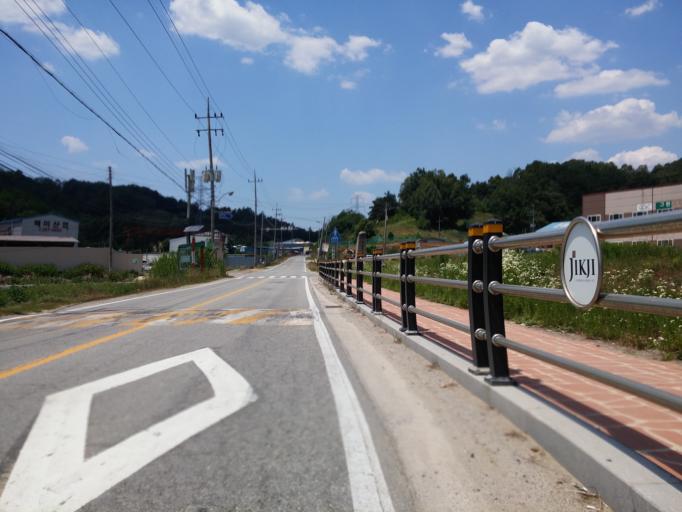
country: KR
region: Chungcheongbuk-do
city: Cheongju-si
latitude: 36.5817
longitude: 127.4465
